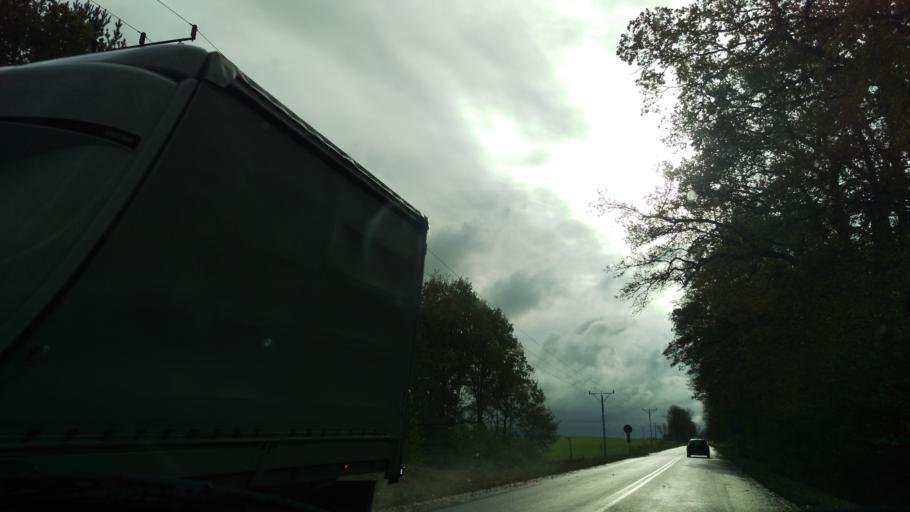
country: PL
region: West Pomeranian Voivodeship
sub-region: Powiat gryficki
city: Gryfice
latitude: 53.8566
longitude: 15.2266
